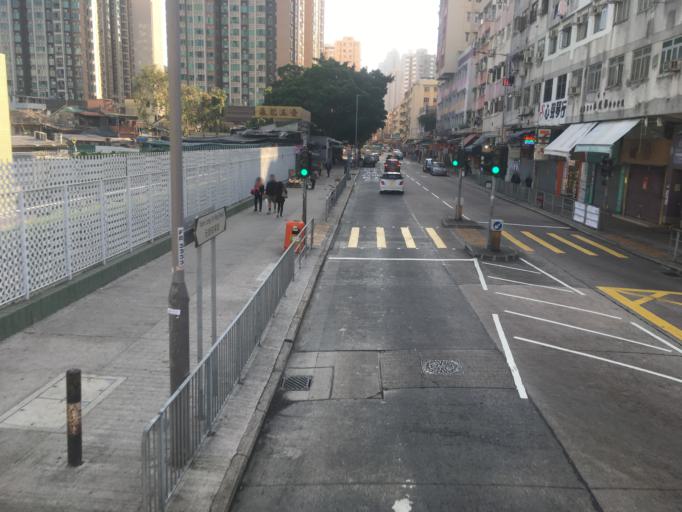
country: HK
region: Yuen Long
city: Yuen Long Kau Hui
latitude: 22.4461
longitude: 114.0258
